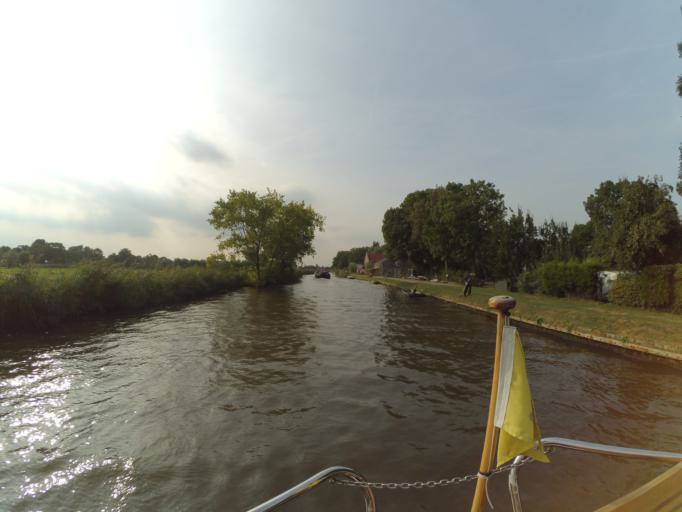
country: NL
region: Utrecht
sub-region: Gemeente Montfoort
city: Montfoort
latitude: 52.0526
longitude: 4.9927
